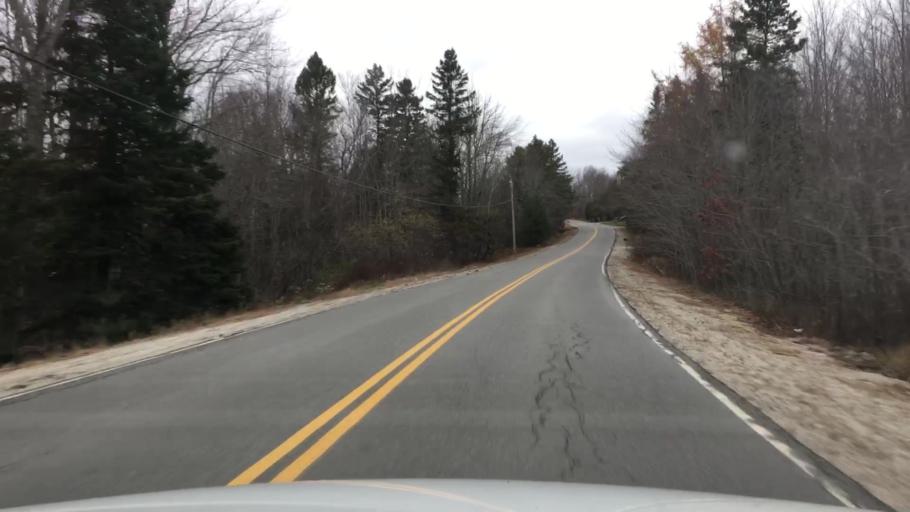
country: US
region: Maine
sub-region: Hancock County
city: Penobscot
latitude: 44.4333
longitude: -68.6306
